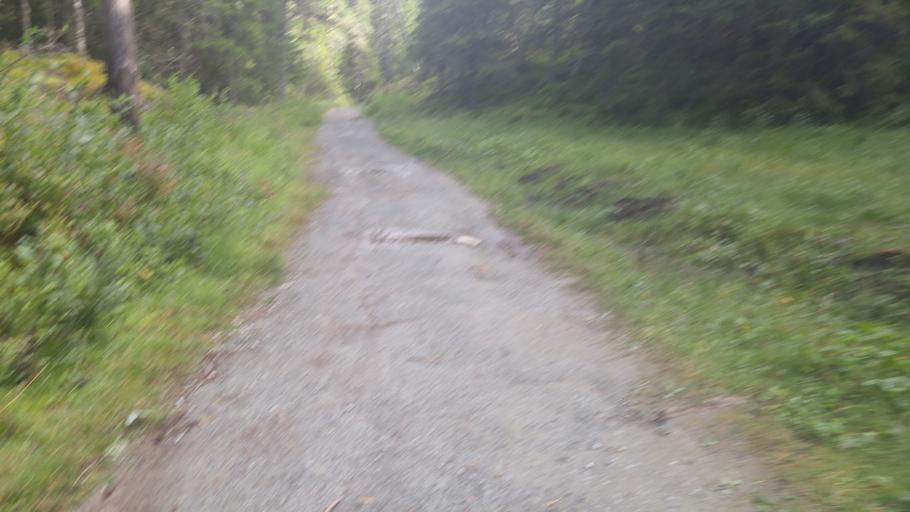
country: NO
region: Sor-Trondelag
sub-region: Trondheim
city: Trondheim
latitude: 63.4133
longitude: 10.3294
